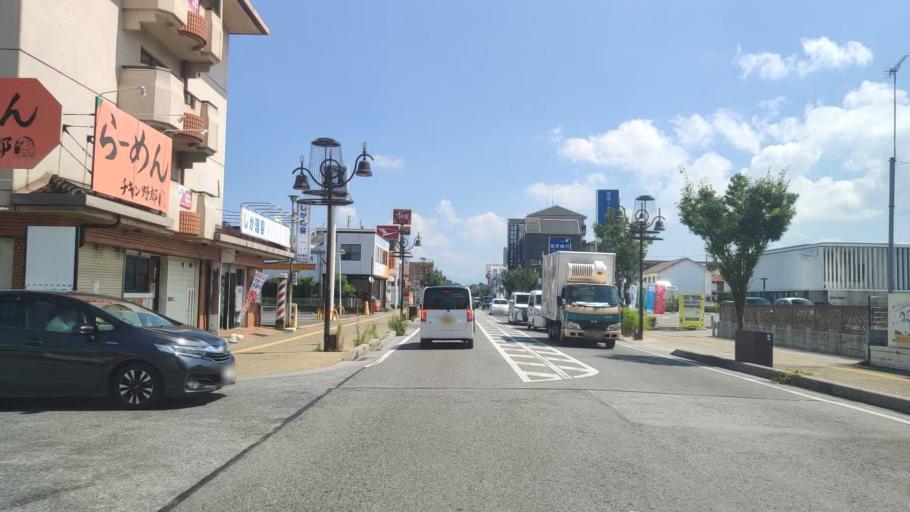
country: JP
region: Shiga Prefecture
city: Hikone
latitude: 35.2611
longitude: 136.2403
